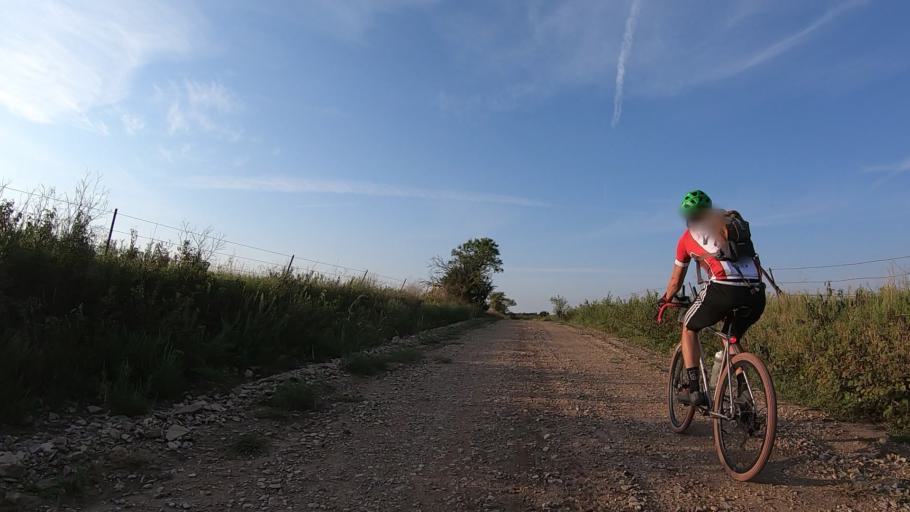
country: US
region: Kansas
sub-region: Marshall County
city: Blue Rapids
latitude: 39.7526
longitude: -96.7507
